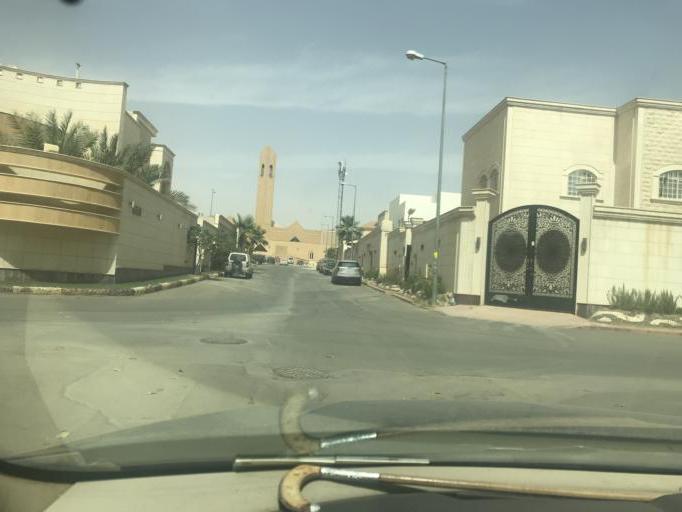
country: SA
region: Ar Riyad
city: Riyadh
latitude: 24.8025
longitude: 46.6622
